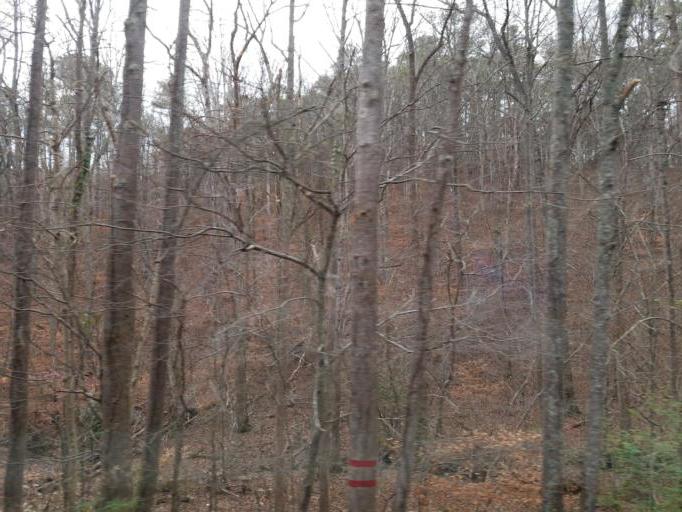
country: US
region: Georgia
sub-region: Cherokee County
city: Holly Springs
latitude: 34.2134
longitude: -84.5573
